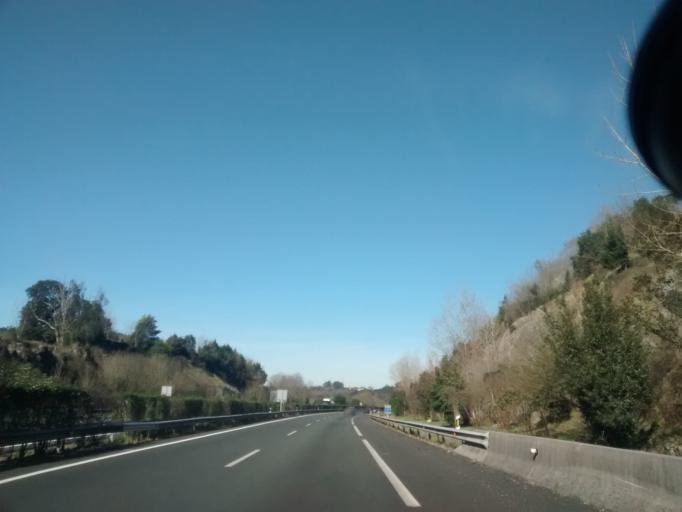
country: ES
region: Cantabria
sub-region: Provincia de Cantabria
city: Entrambasaguas
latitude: 43.3907
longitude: -3.6915
